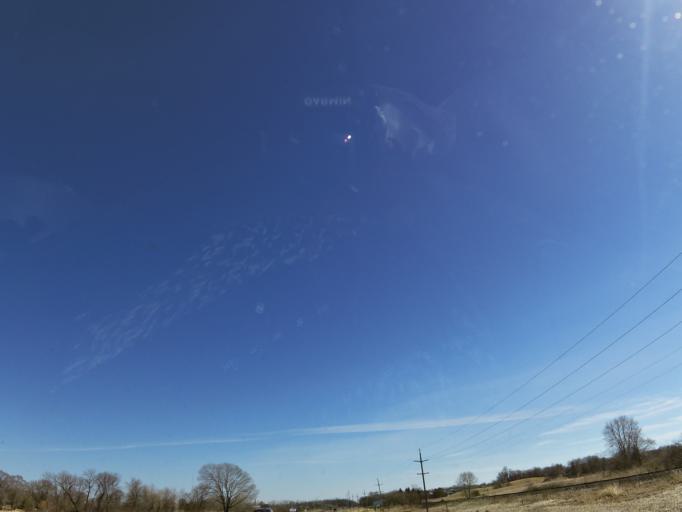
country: US
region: Minnesota
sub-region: Wright County
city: Buffalo
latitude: 45.1938
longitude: -93.8954
